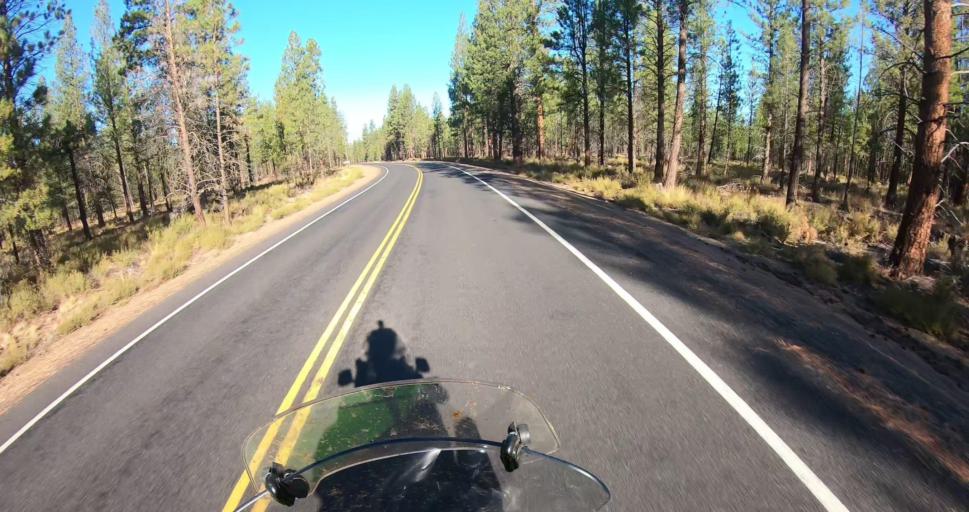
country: US
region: Oregon
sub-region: Deschutes County
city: La Pine
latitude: 43.7335
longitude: -121.4393
